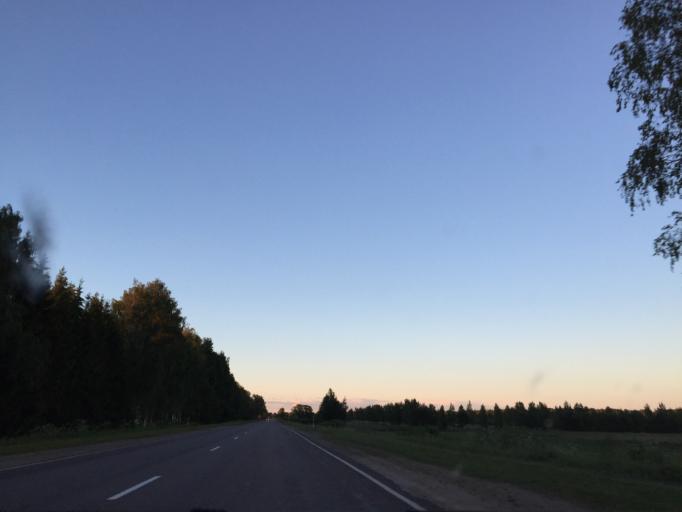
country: LV
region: Jaunpiebalga
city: Jaunpiebalga
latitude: 57.4471
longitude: 26.2168
